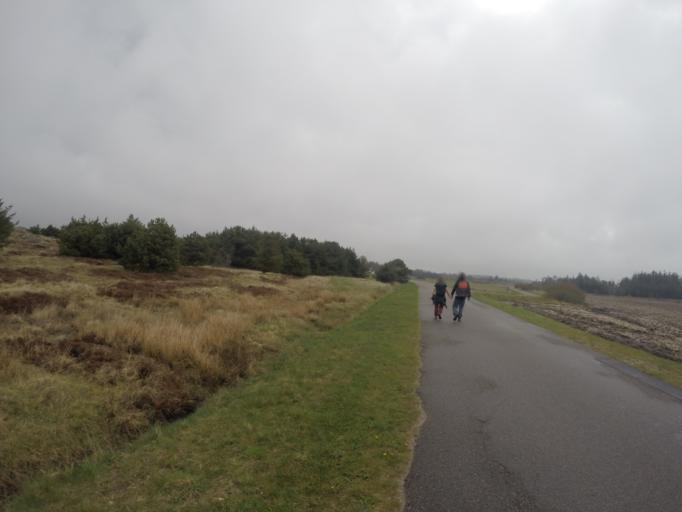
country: DK
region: North Denmark
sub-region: Thisted Kommune
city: Hanstholm
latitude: 57.0360
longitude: 8.5278
